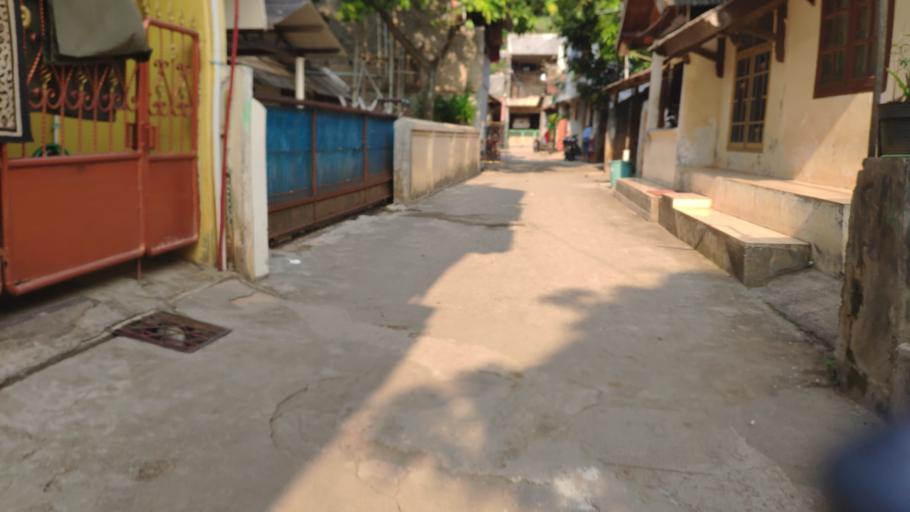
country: ID
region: West Java
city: Pamulang
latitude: -6.3036
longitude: 106.8076
